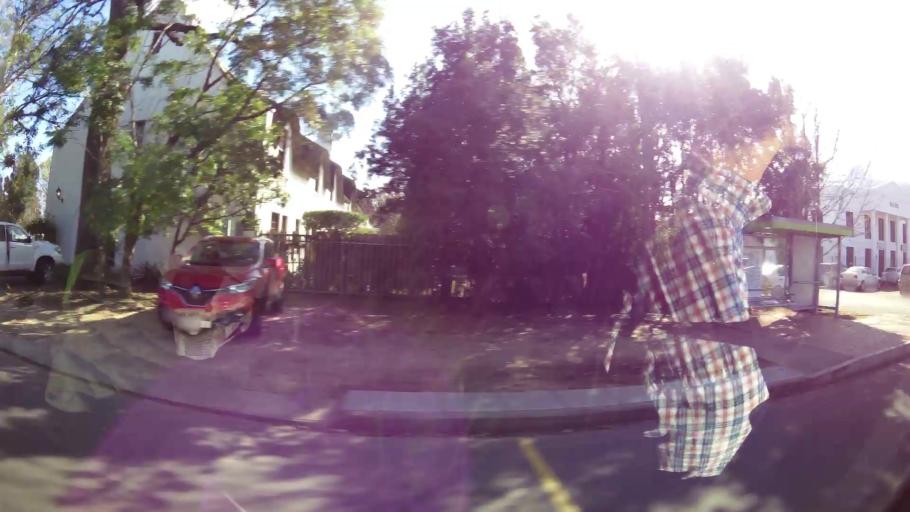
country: ZA
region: Western Cape
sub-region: Eden District Municipality
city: George
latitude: -33.9584
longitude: 22.4613
